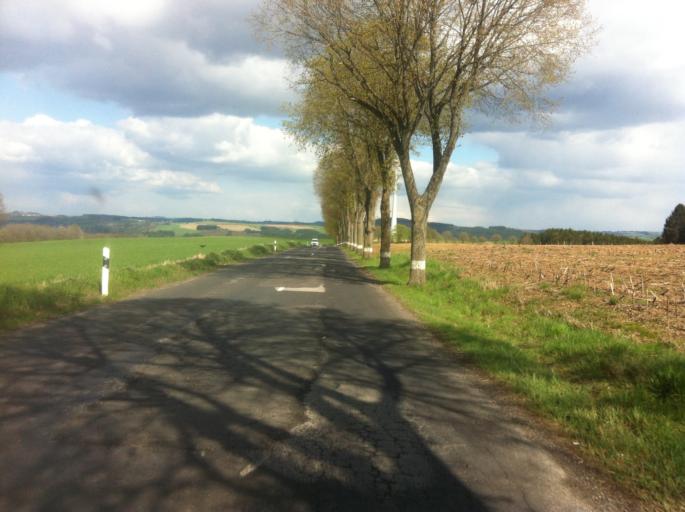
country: LU
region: Diekirch
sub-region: Canton de Clervaux
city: Hosingen
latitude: 50.0512
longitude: 6.0871
